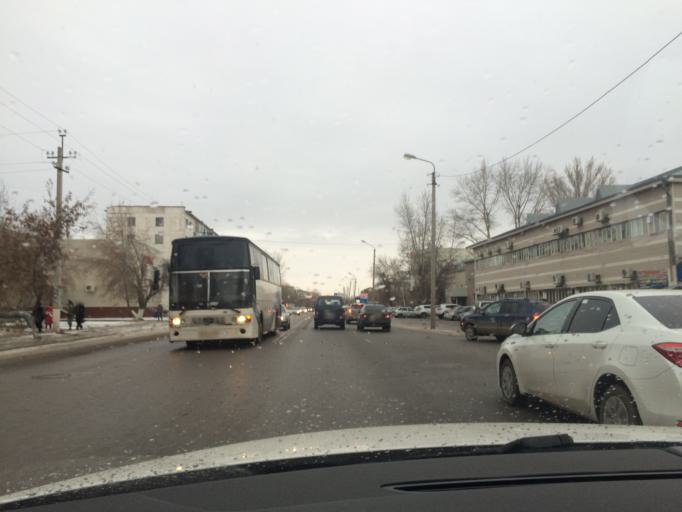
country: KZ
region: Astana Qalasy
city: Astana
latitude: 51.1844
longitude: 71.4219
